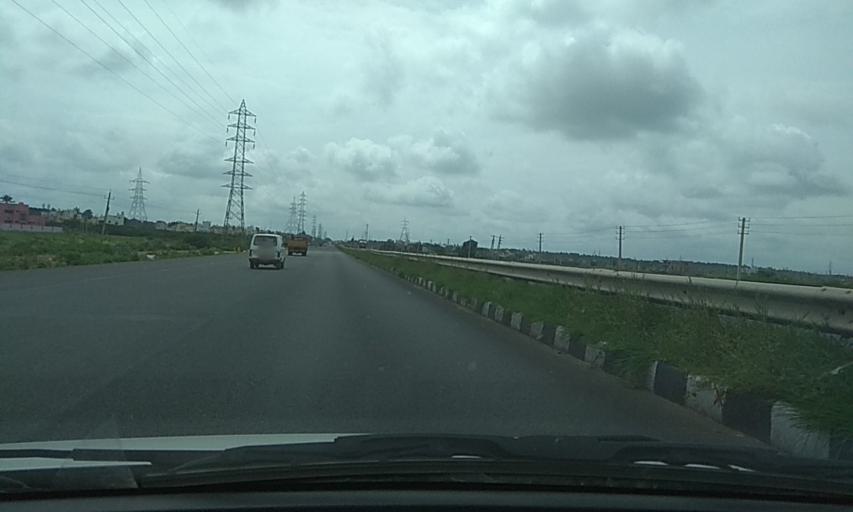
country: IN
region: Karnataka
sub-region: Davanagere
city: Harihar
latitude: 14.4378
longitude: 75.9074
